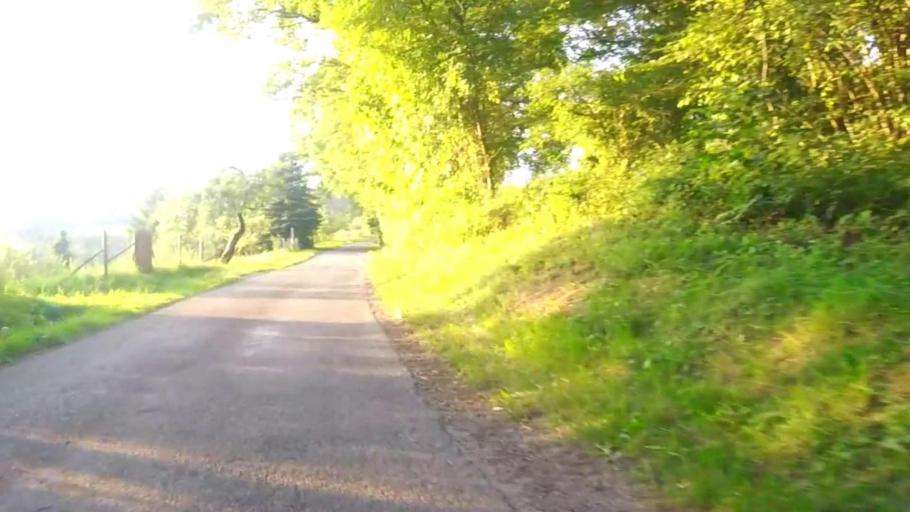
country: DE
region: Baden-Wuerttemberg
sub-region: Regierungsbezirk Stuttgart
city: Oppenweiler
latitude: 48.9982
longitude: 9.4591
